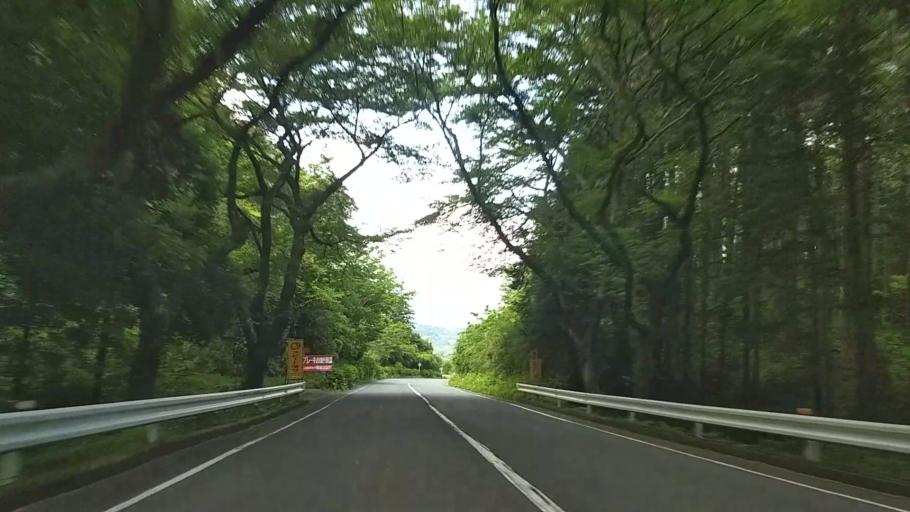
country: JP
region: Kanagawa
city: Odawara
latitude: 35.2300
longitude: 139.1235
